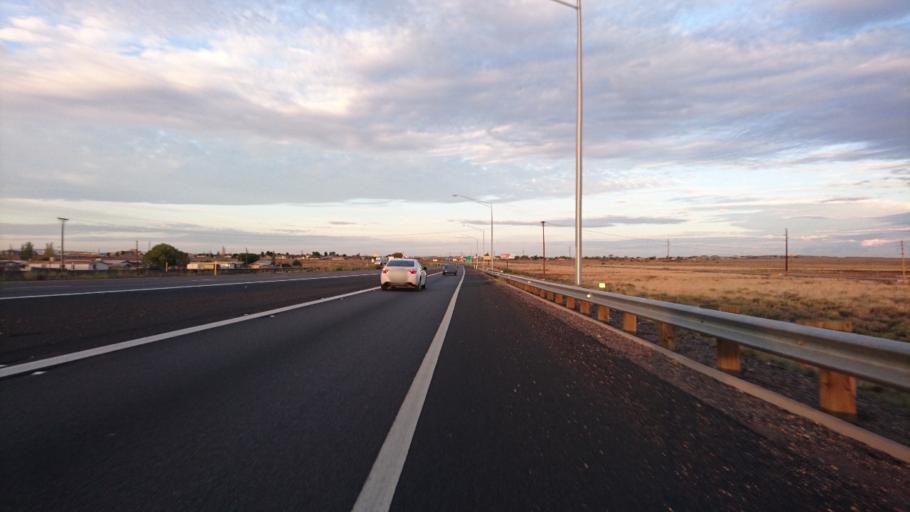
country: US
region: Arizona
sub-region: Navajo County
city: Winslow
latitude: 35.0397
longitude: -110.7034
